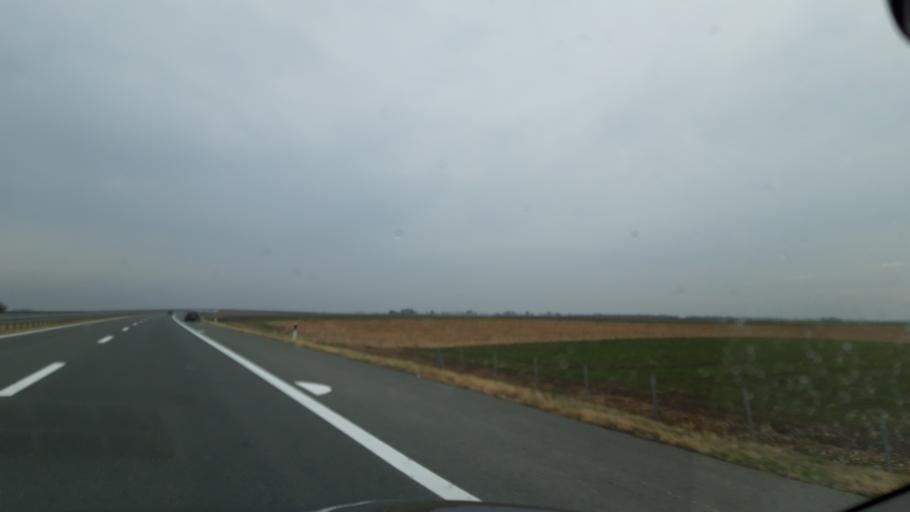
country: RS
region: Autonomna Pokrajina Vojvodina
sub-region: Severnobacki Okrug
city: Mali Igos
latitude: 45.7363
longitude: 19.7039
